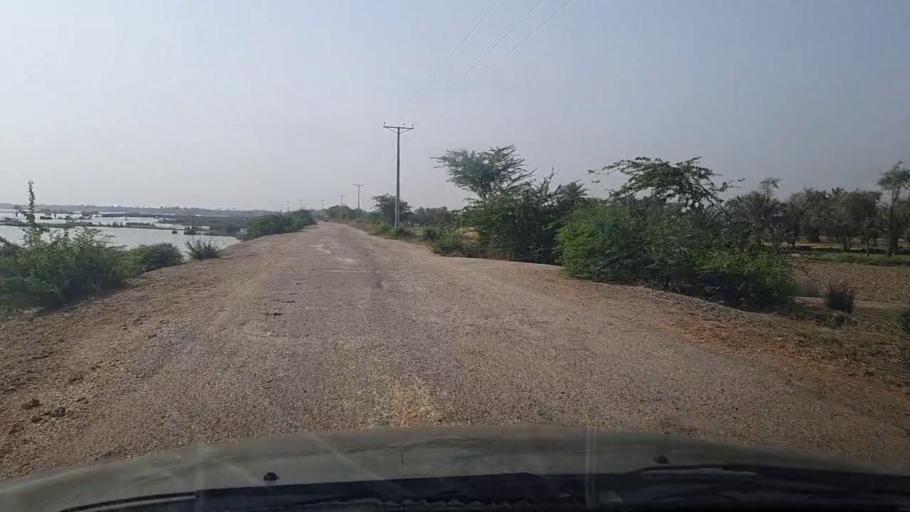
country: PK
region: Sindh
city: Kot Diji
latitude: 27.2937
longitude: 68.6443
